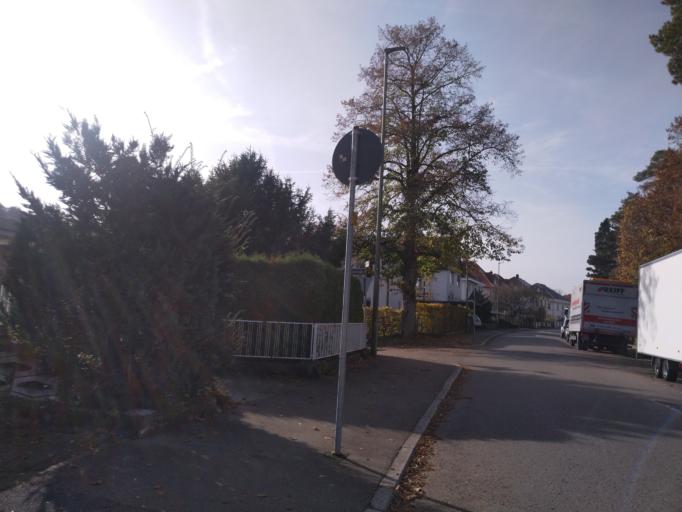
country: DE
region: Baden-Wuerttemberg
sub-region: Karlsruhe Region
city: Pforzheim
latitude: 48.8770
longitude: 8.6946
